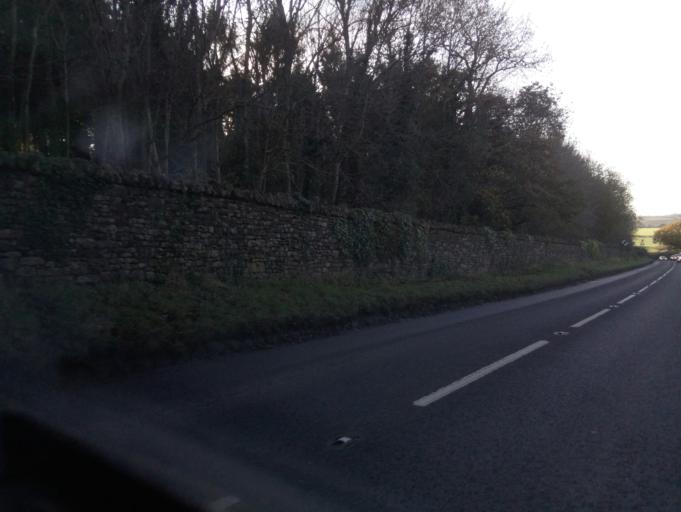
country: GB
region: England
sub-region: Somerset
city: Milborne Port
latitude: 50.9635
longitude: -2.4761
